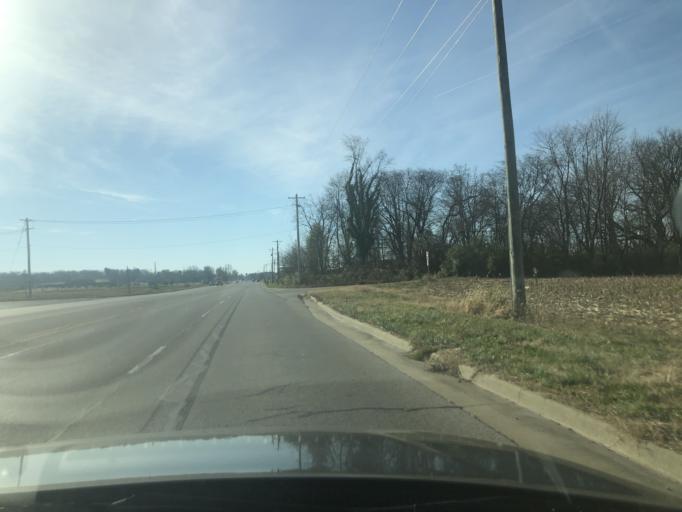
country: US
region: Indiana
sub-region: Warrick County
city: Newburgh
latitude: 37.9847
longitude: -87.4412
